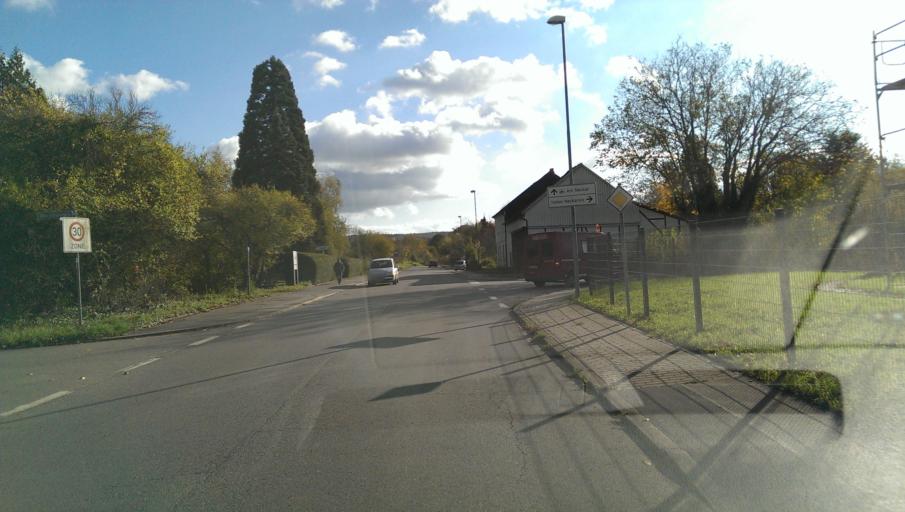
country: DE
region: Baden-Wuerttemberg
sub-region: Karlsruhe Region
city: Obrigheim
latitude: 49.3381
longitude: 9.1057
